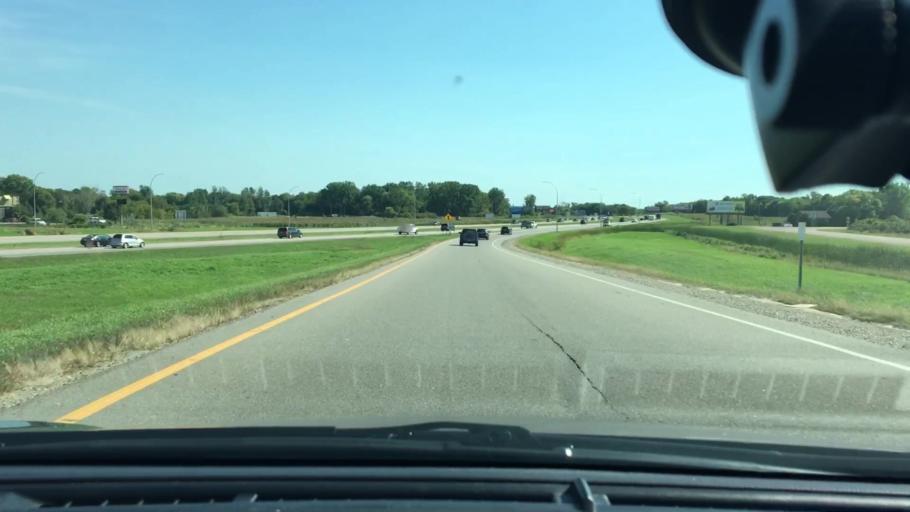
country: US
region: Minnesota
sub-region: Wright County
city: Albertville
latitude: 45.2367
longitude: -93.6486
